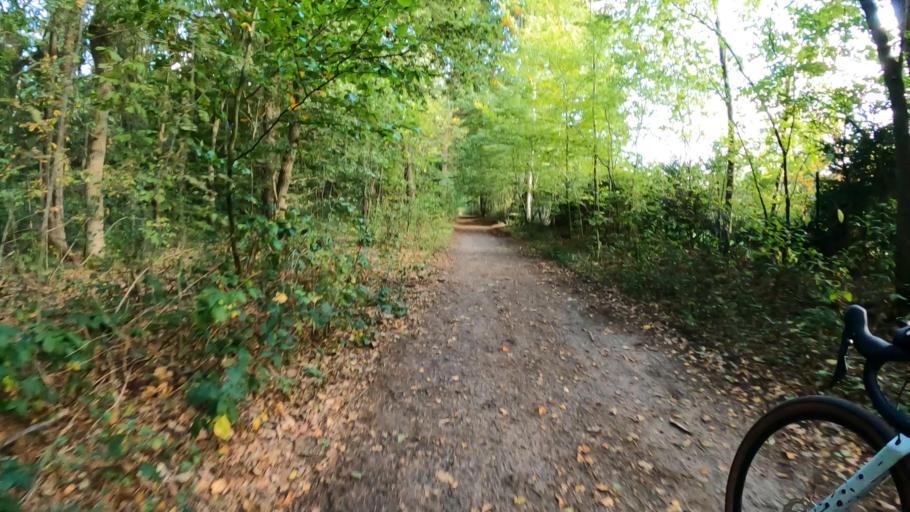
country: DE
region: Schleswig-Holstein
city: Hartenholm
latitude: 53.9027
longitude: 10.0673
